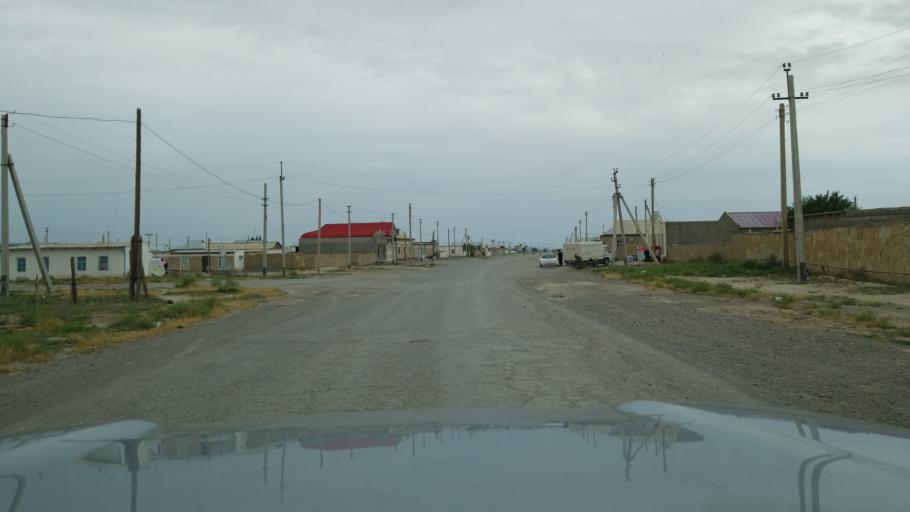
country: TM
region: Balkan
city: Serdar
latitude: 38.9910
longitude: 56.2775
